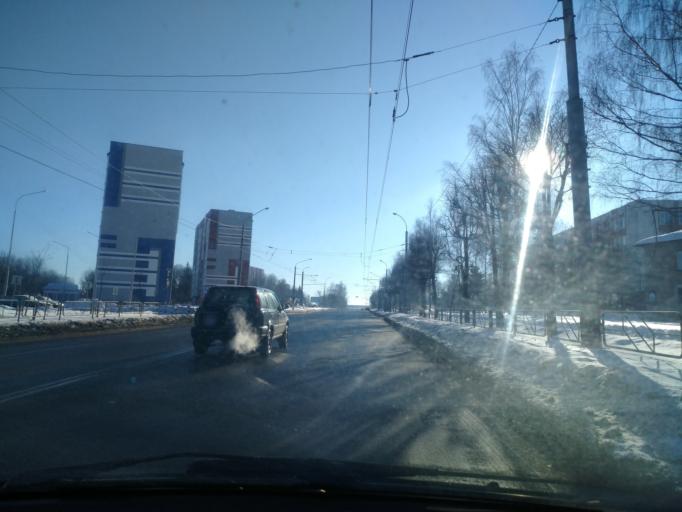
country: BY
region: Mogilev
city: Buynichy
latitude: 53.8963
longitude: 30.2958
